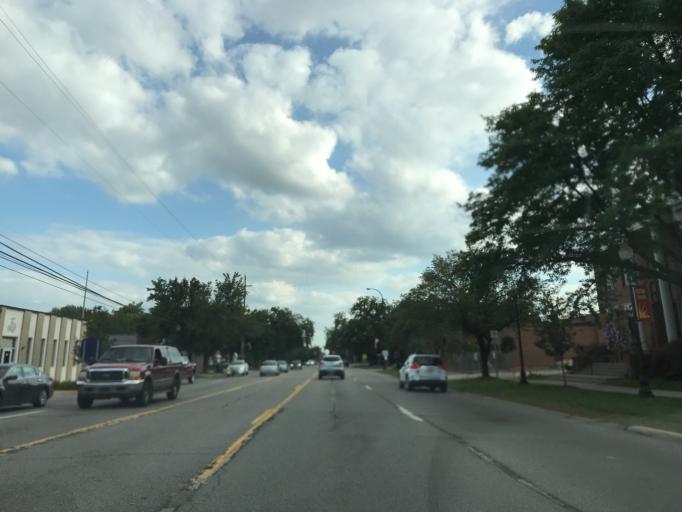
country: US
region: Michigan
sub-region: Wayne County
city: Redford
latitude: 42.3988
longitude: -83.2959
